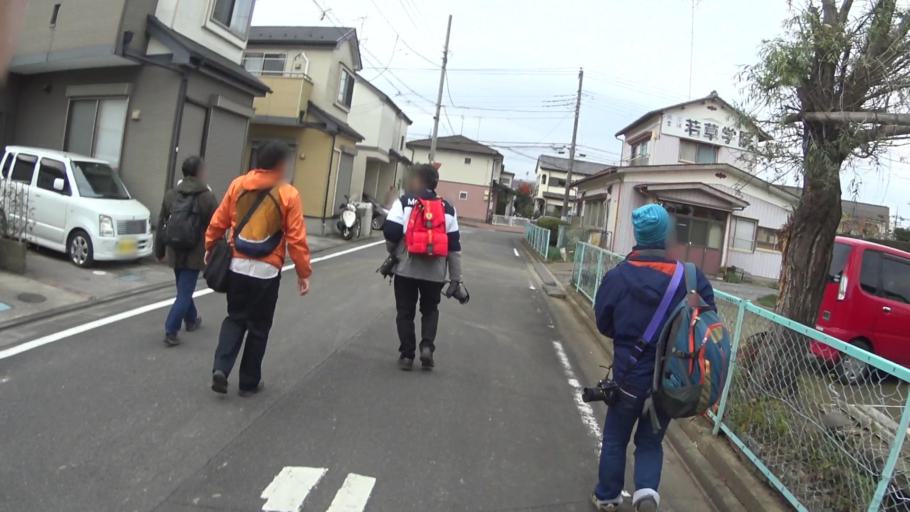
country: JP
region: Chiba
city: Nagareyama
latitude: 35.8399
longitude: 139.8853
